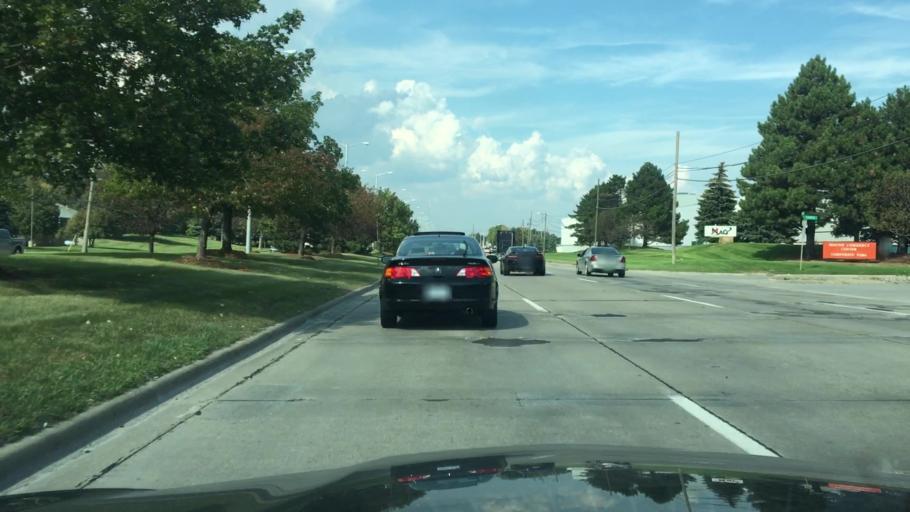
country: US
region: Michigan
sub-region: Macomb County
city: Sterling Heights
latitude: 42.5592
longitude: -83.0487
